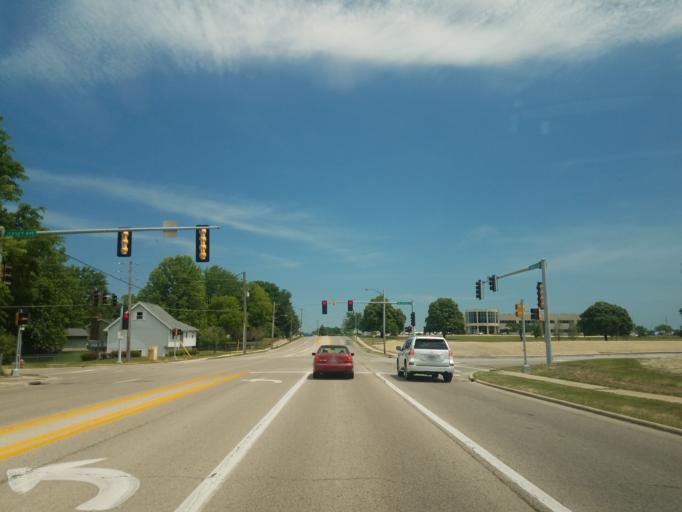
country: US
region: Illinois
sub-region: McLean County
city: Normal
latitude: 40.4990
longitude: -88.9595
